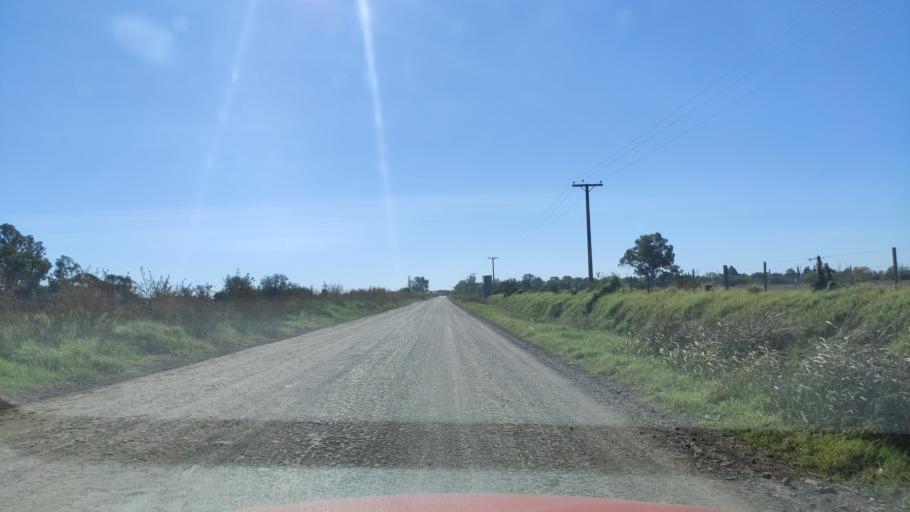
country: AR
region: Cordoba
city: Leones
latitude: -32.6683
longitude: -62.3122
